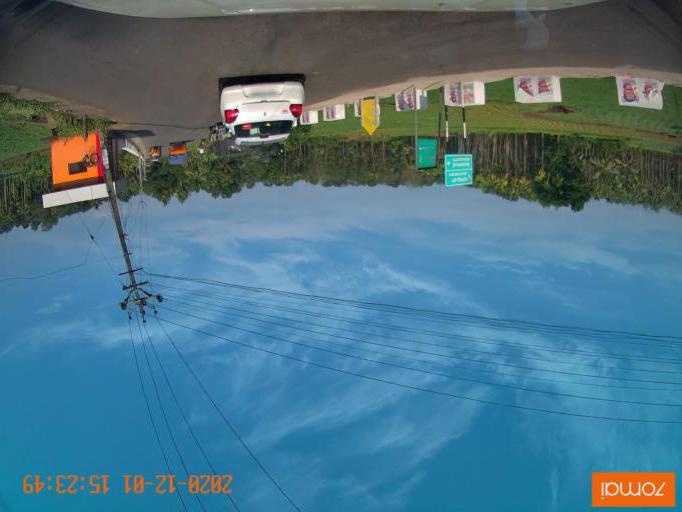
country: IN
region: Kerala
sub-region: Ernakulam
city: Muvattupuzha
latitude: 9.9526
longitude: 76.5520
